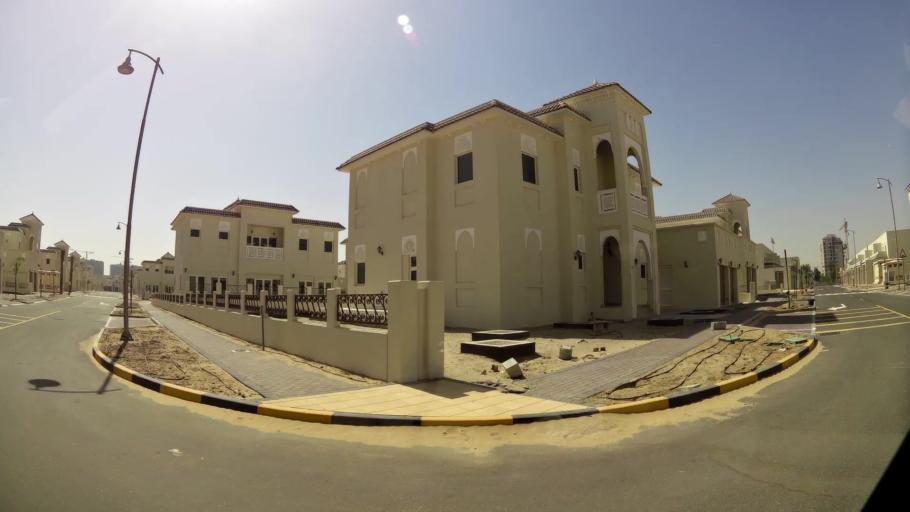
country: AE
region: Dubai
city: Dubai
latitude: 25.0243
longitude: 55.1486
